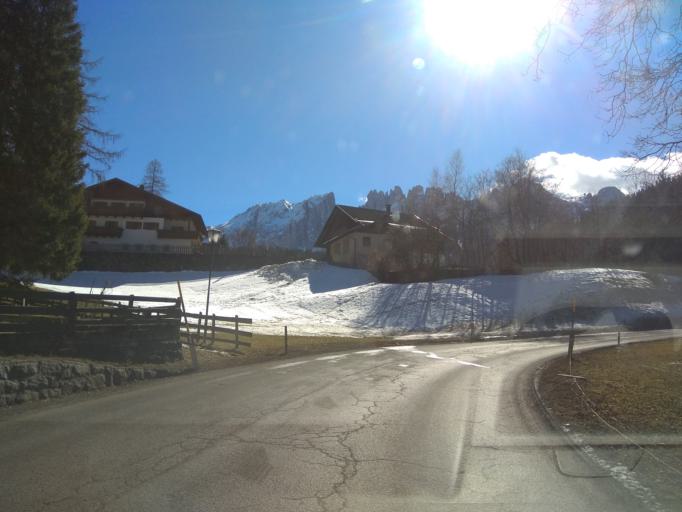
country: IT
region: Trentino-Alto Adige
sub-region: Bolzano
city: Nova Levante
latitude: 46.4214
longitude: 11.5585
